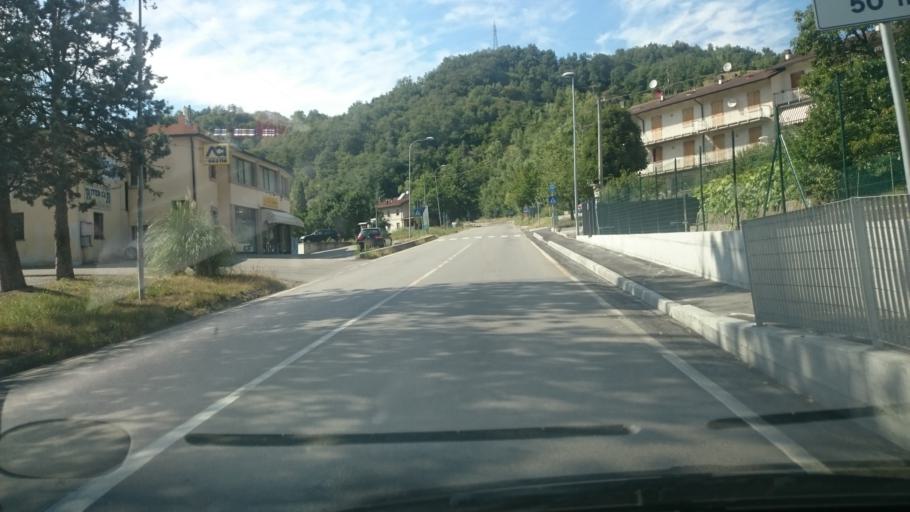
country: IT
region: Emilia-Romagna
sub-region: Provincia di Modena
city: Montefiorino
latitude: 44.4071
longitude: 10.6154
